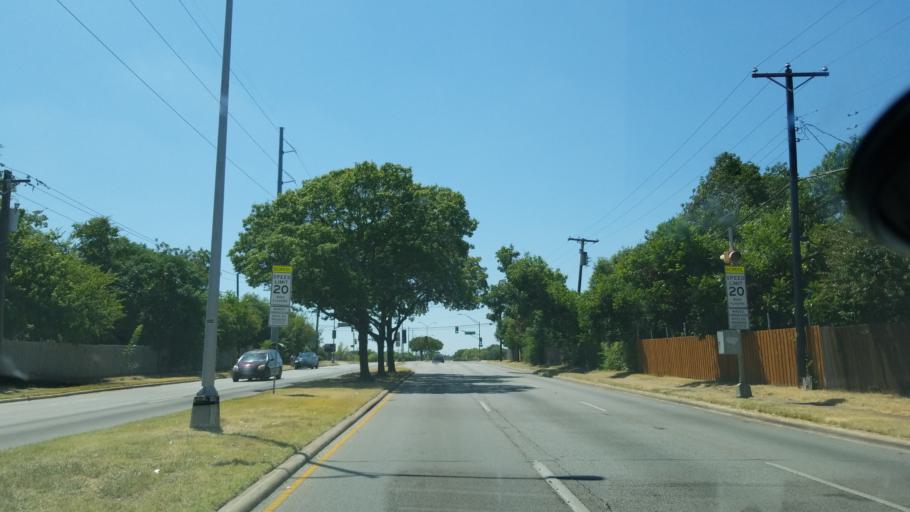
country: US
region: Texas
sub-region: Dallas County
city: Cockrell Hill
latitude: 32.7205
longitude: -96.8988
